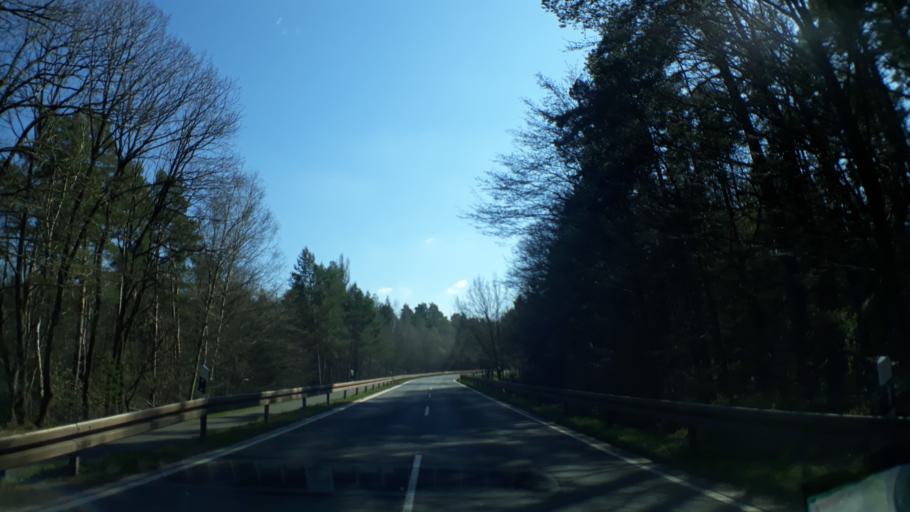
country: DE
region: North Rhine-Westphalia
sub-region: Regierungsbezirk Koln
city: Mechernich
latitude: 50.5803
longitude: 6.6528
